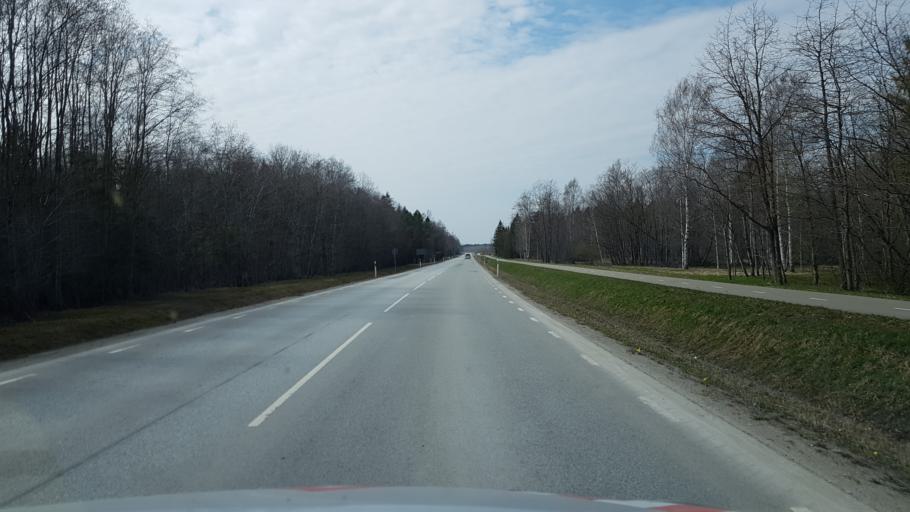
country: EE
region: Ida-Virumaa
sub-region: Kivioli linn
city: Kivioli
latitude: 59.3551
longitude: 26.9241
